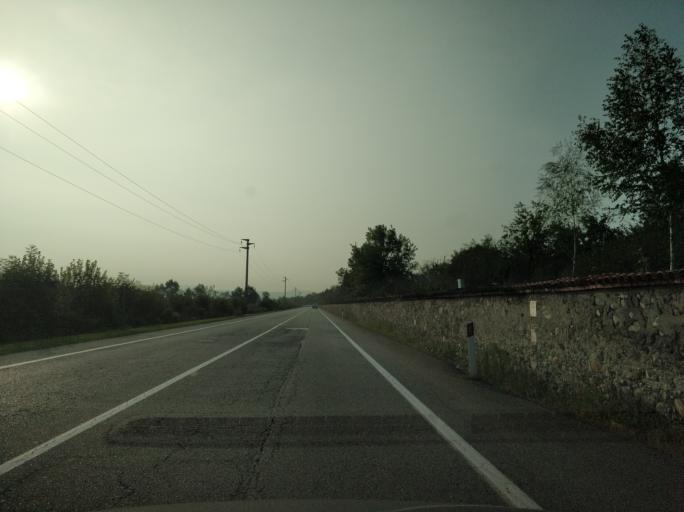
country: IT
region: Piedmont
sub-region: Provincia di Torino
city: Druento
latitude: 45.1668
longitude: 7.5952
